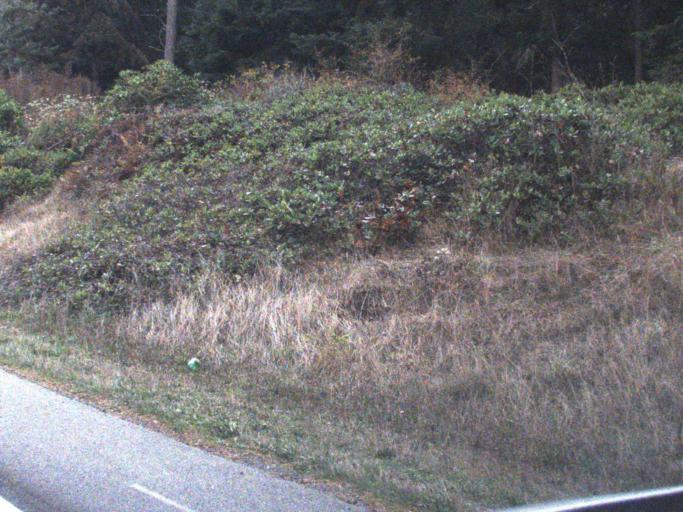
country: US
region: Washington
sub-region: Island County
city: Freeland
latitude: 48.0526
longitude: -122.5669
